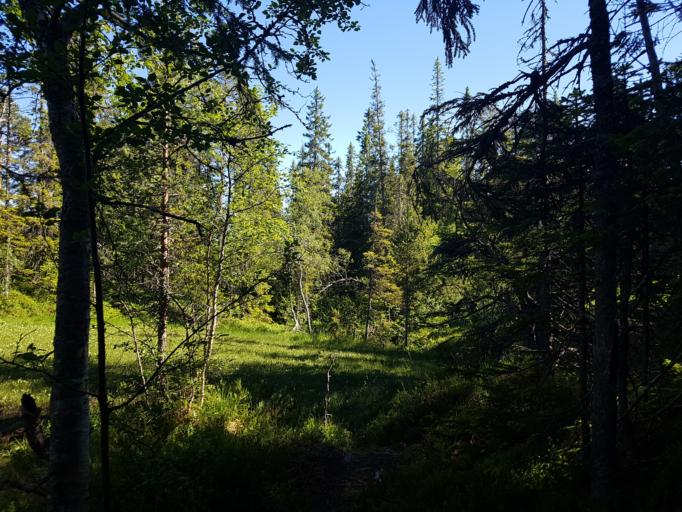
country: NO
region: Sor-Trondelag
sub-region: Trondheim
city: Trondheim
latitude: 63.4384
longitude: 10.2686
